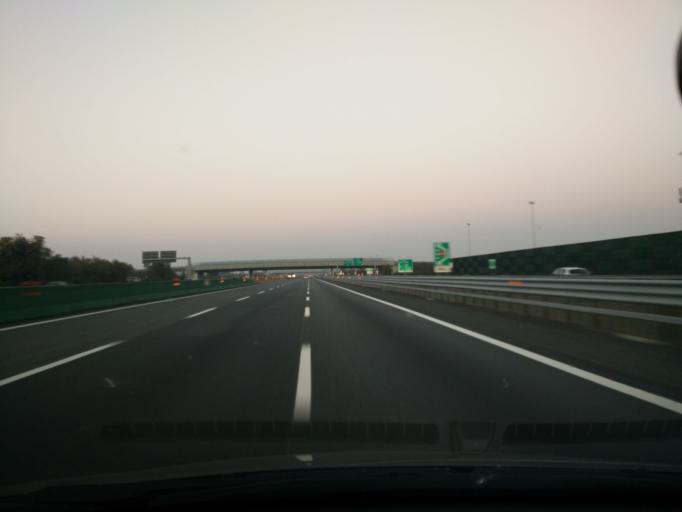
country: IT
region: Piedmont
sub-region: Provincia di Vercelli
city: Santhia
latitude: 45.3742
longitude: 8.1301
